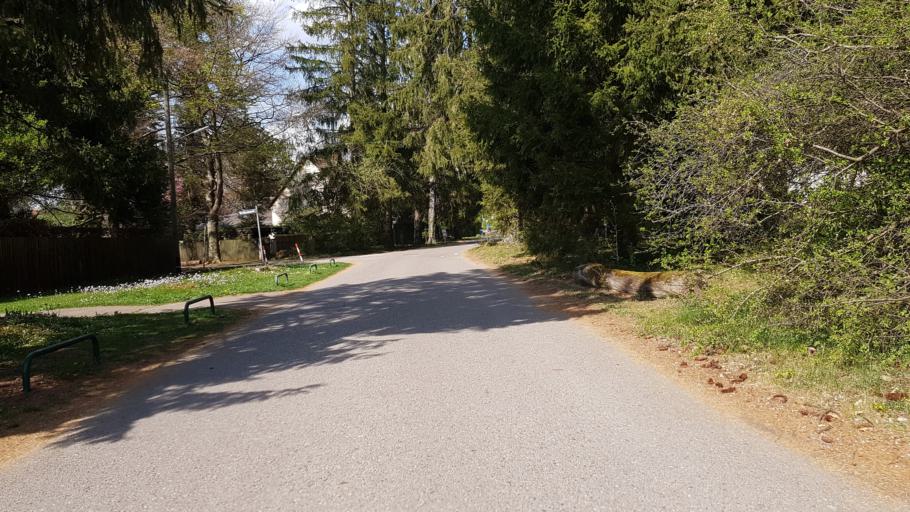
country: DE
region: Bavaria
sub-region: Upper Bavaria
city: Karlsfeld
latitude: 48.1767
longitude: 11.4944
